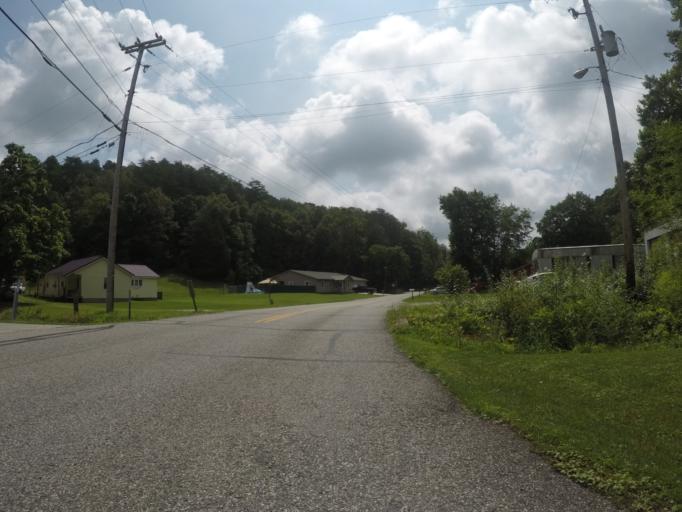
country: US
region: Kentucky
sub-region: Boyd County
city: Meads
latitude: 38.4151
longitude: -82.6841
